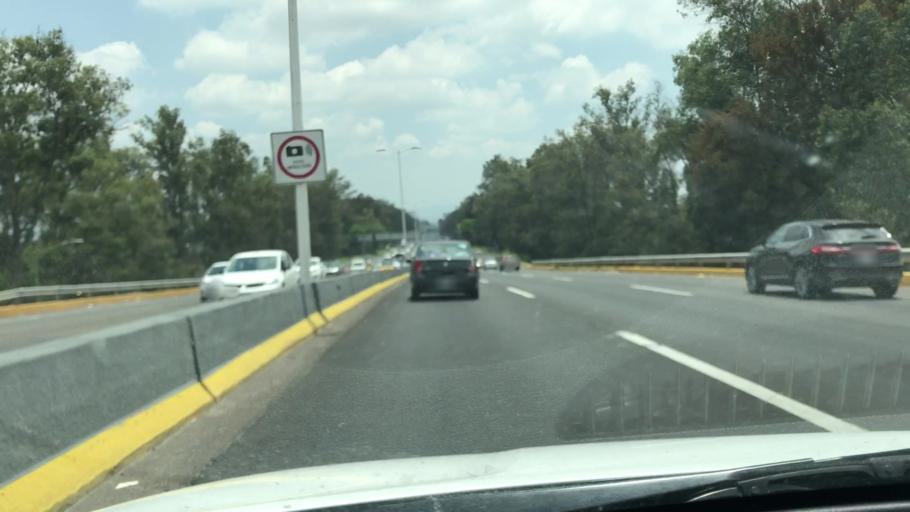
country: MX
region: Jalisco
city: Zapopan2
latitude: 20.7000
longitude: -103.4516
